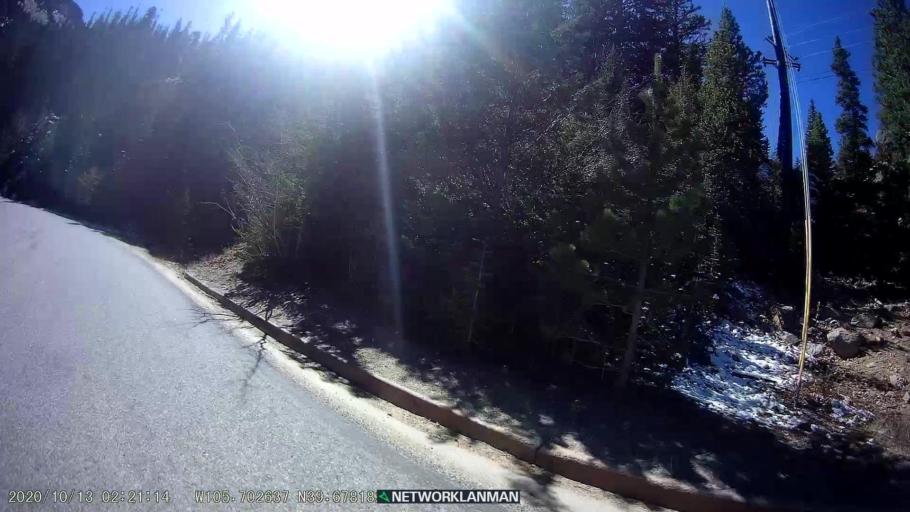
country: US
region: Colorado
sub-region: Clear Creek County
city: Georgetown
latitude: 39.6773
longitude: -105.7013
